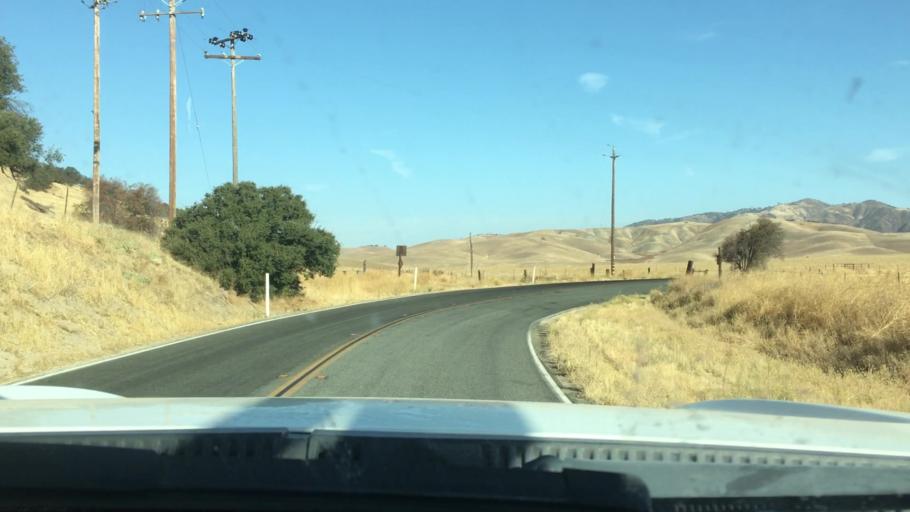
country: US
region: California
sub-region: Monterey County
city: King City
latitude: 36.3850
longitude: -121.0054
